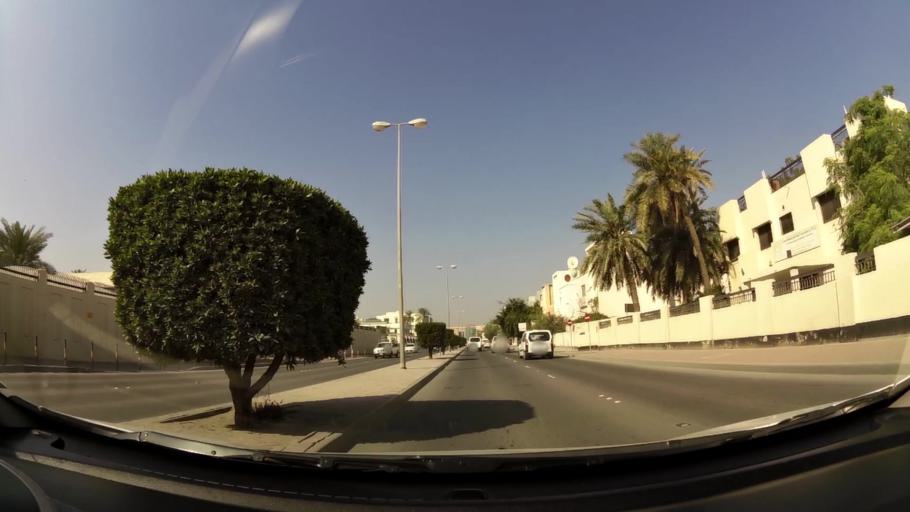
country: BH
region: Manama
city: Manama
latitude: 26.2202
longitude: 50.5820
